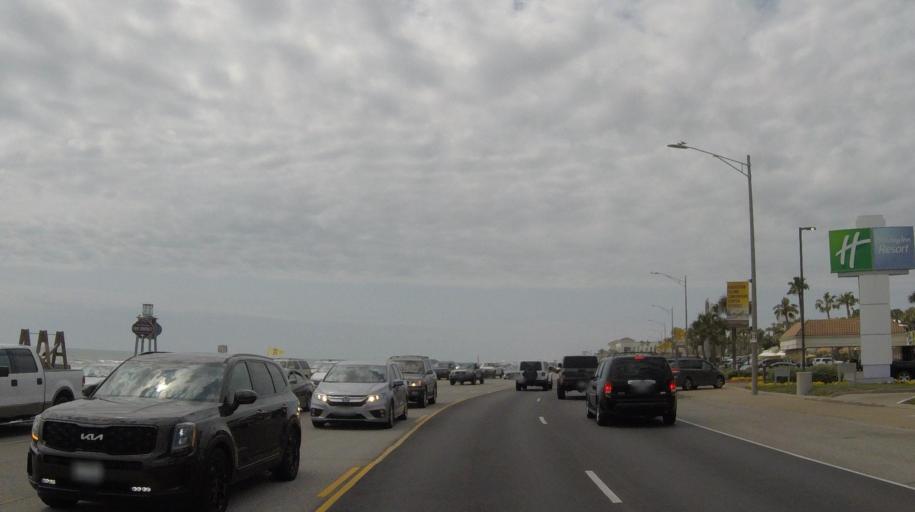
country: US
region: Texas
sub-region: Galveston County
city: Galveston
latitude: 29.2725
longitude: -94.8154
